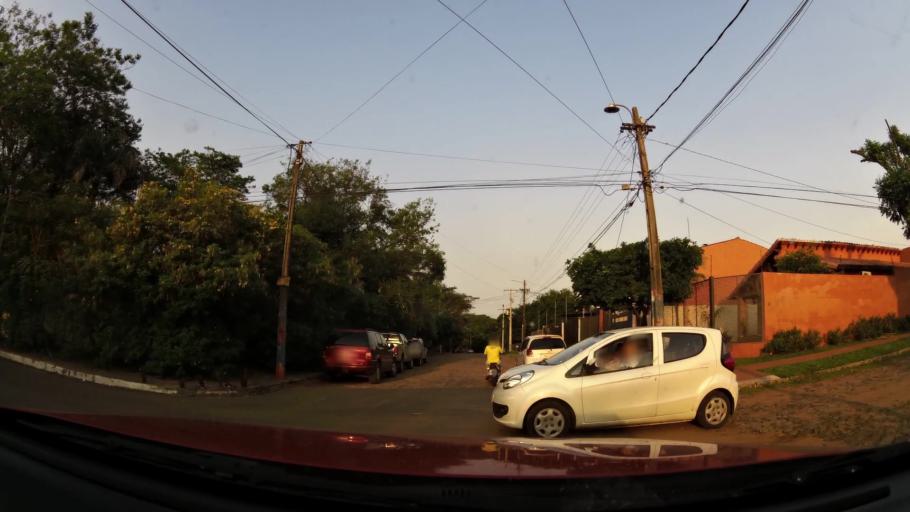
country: PY
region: Central
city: Lambare
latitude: -25.3524
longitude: -57.6032
